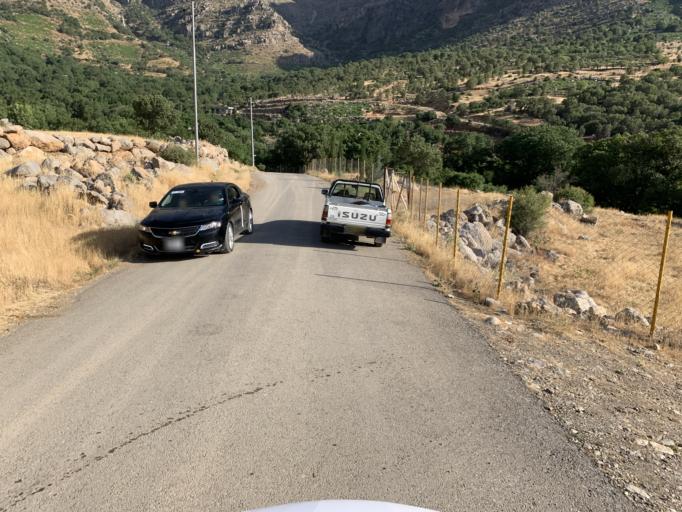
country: IQ
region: As Sulaymaniyah
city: Qeladize
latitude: 35.9901
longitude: 45.2000
